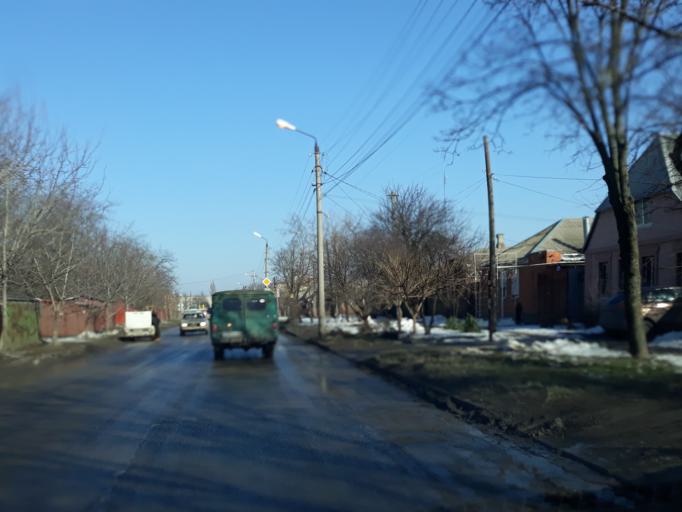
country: RU
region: Rostov
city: Taganrog
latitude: 47.2265
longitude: 38.8762
